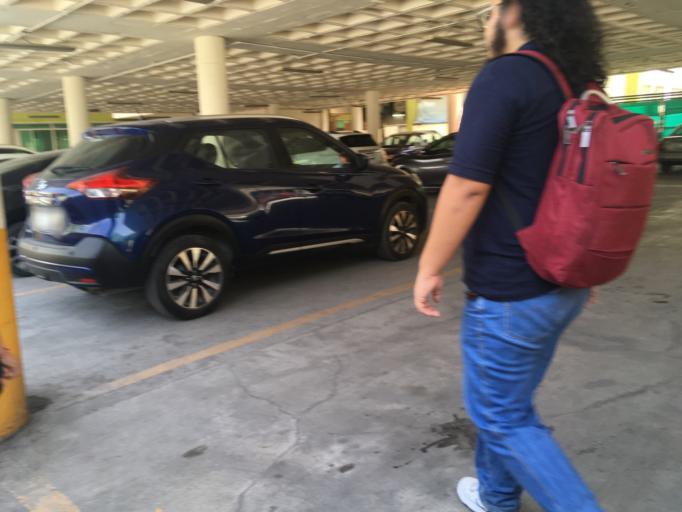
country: MX
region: Nuevo Leon
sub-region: San Nicolas de los Garza
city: San Nicolas de los Garza
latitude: 25.7268
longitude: -100.3111
